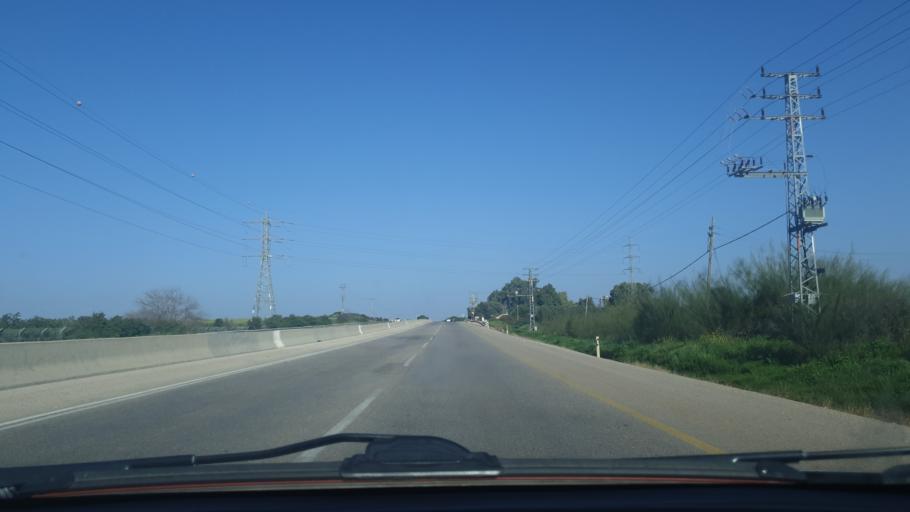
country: IL
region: Central District
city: Bet Dagan
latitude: 31.9835
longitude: 34.8336
